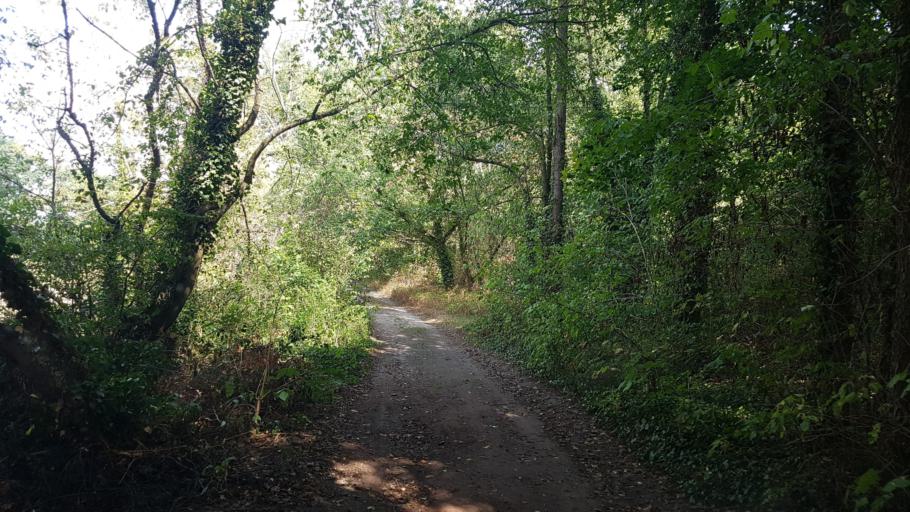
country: DE
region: Brandenburg
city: Altdobern
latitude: 51.6564
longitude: 14.0173
